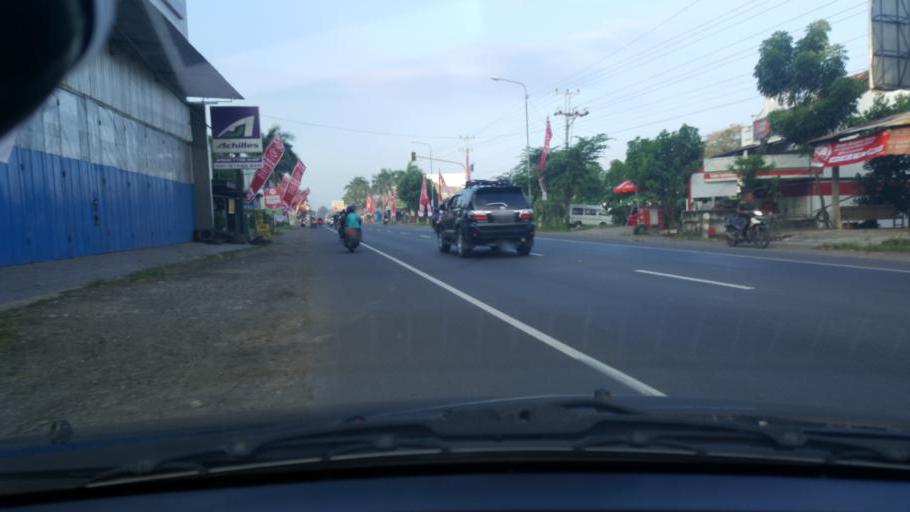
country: ID
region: Central Java
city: Gemiring
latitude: -6.7831
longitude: 110.9864
